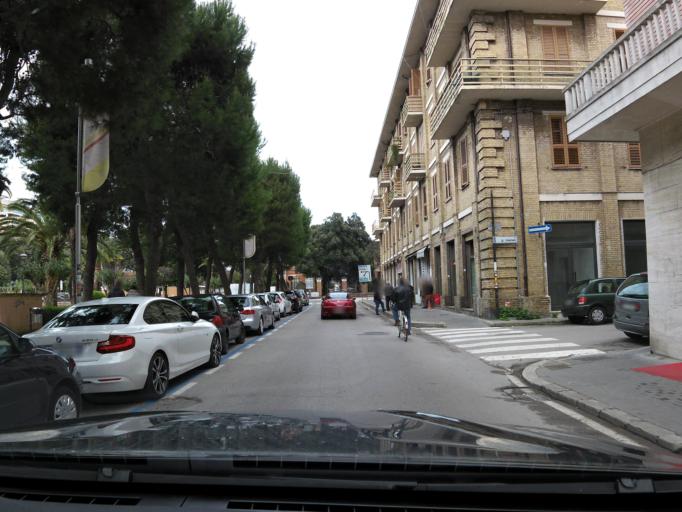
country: IT
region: The Marches
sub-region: Provincia di Macerata
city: Portocivitanova
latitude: 43.3072
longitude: 13.7306
